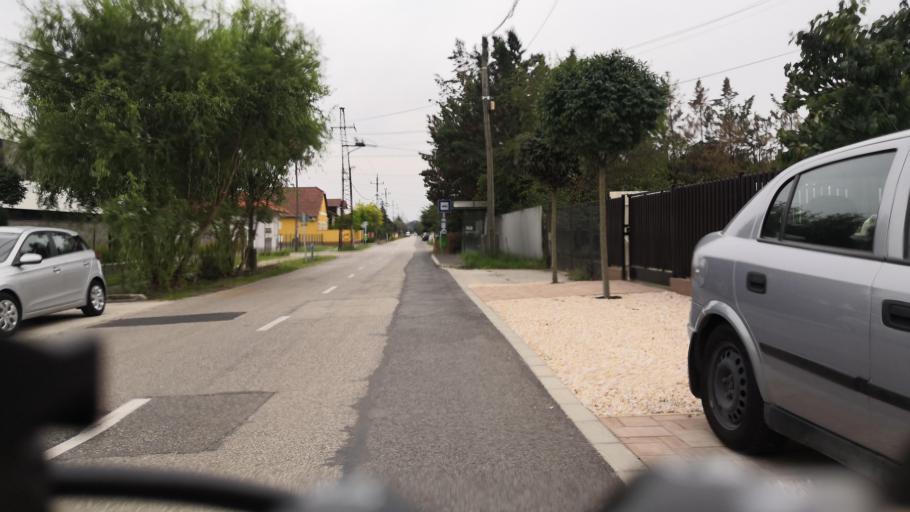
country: HU
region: Csongrad
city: Szeged
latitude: 46.2890
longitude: 20.1637
